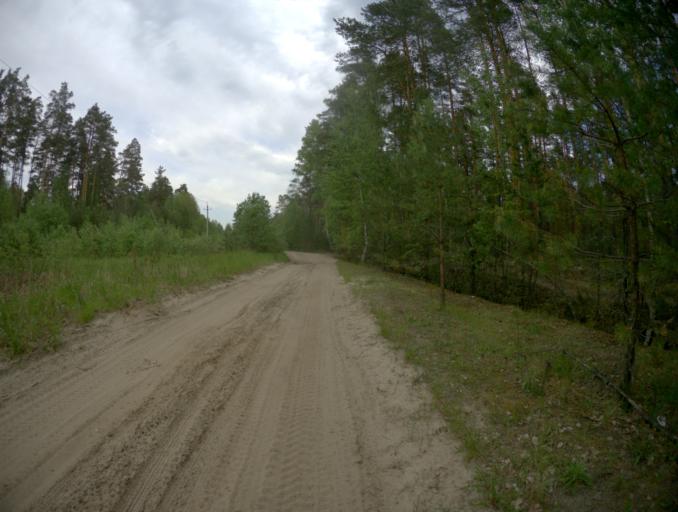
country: RU
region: Vladimir
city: Ivanishchi
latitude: 55.7665
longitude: 40.4147
